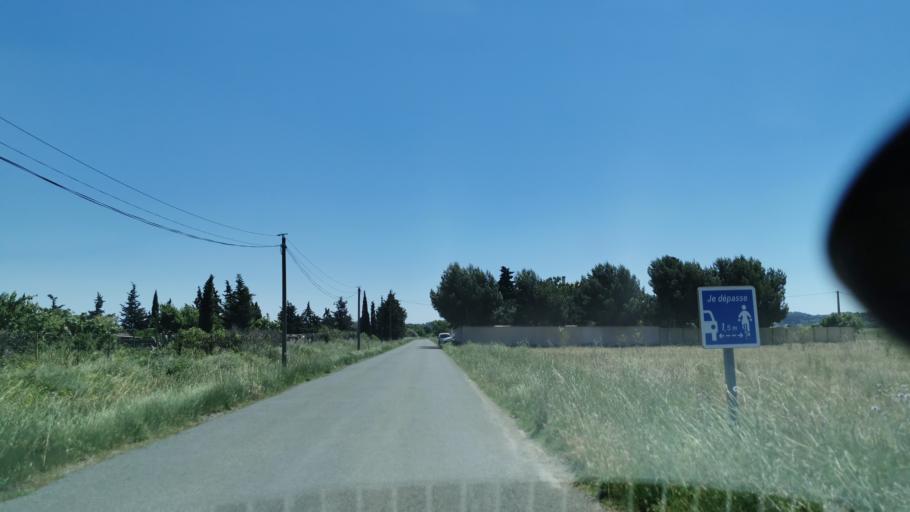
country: FR
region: Languedoc-Roussillon
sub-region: Departement de l'Aude
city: Marcorignan
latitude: 43.2447
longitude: 2.9079
